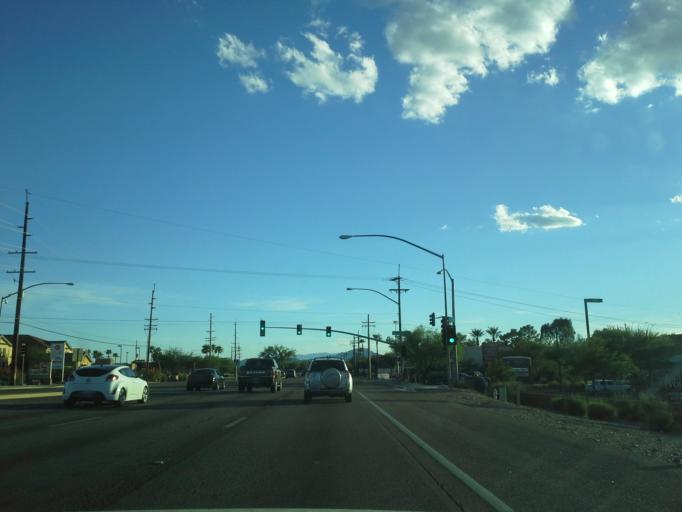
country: US
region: Arizona
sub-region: Pima County
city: Casas Adobes
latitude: 32.3163
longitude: -110.9765
